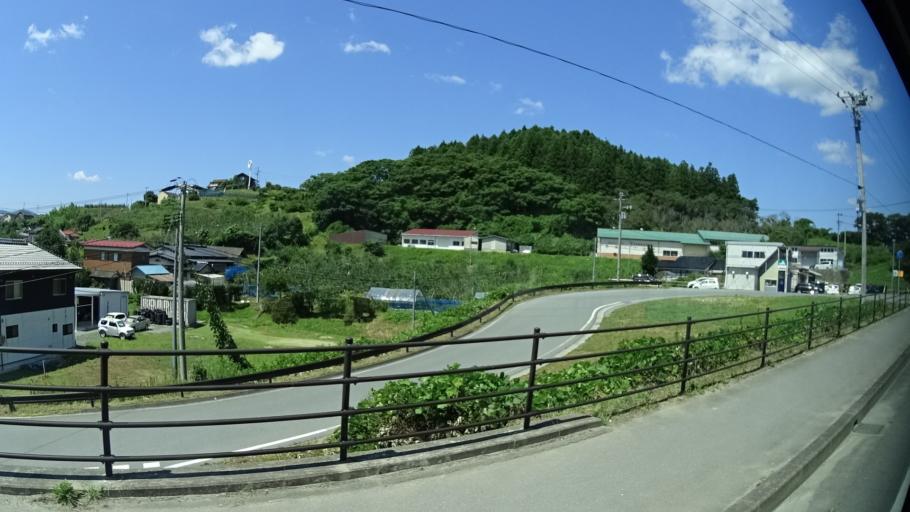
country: JP
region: Iwate
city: Ofunato
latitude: 39.0140
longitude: 141.6688
